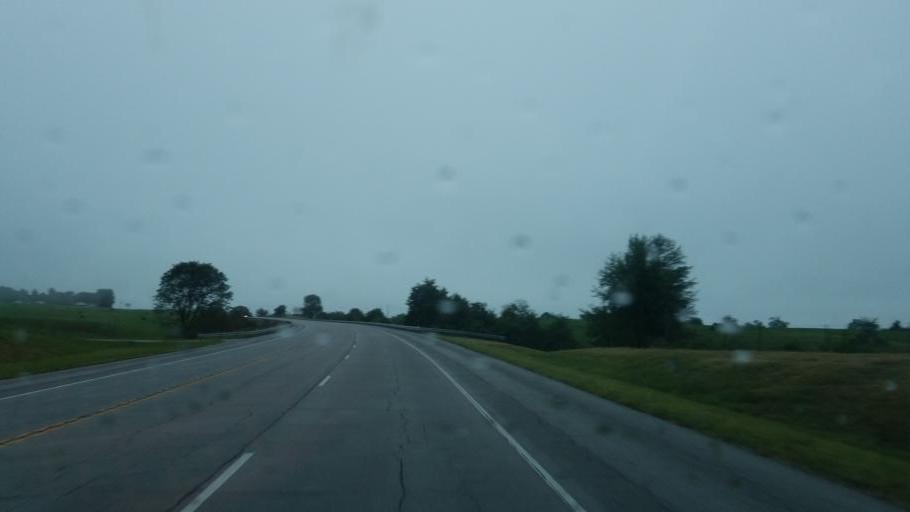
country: US
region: Kentucky
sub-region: Fleming County
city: Flemingsburg
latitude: 38.3961
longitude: -83.7154
